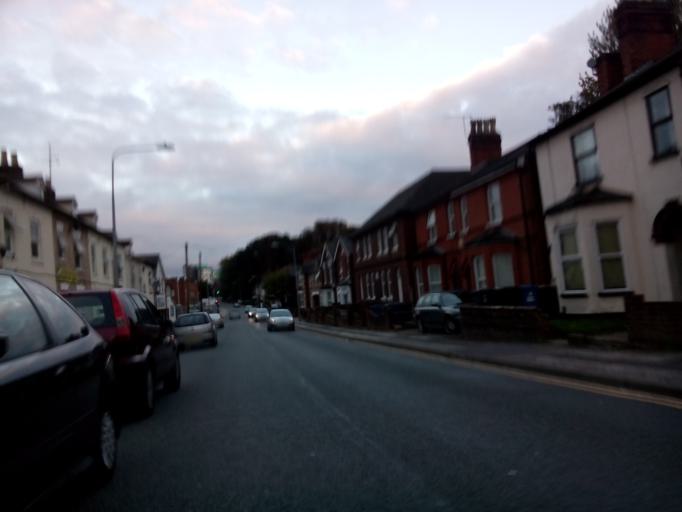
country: GB
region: England
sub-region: Suffolk
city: Ipswich
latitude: 52.0507
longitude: 1.1486
